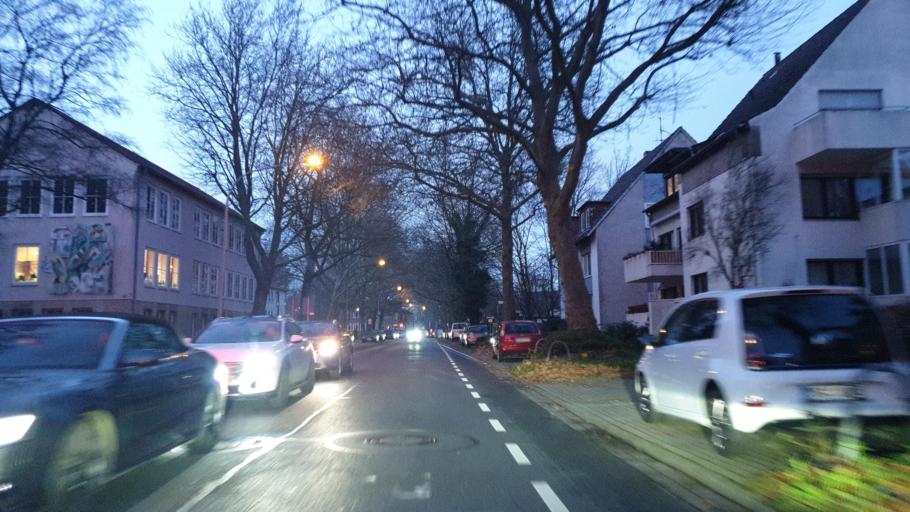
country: DE
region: Lower Saxony
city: Osnabrueck
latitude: 52.2704
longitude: 8.0207
